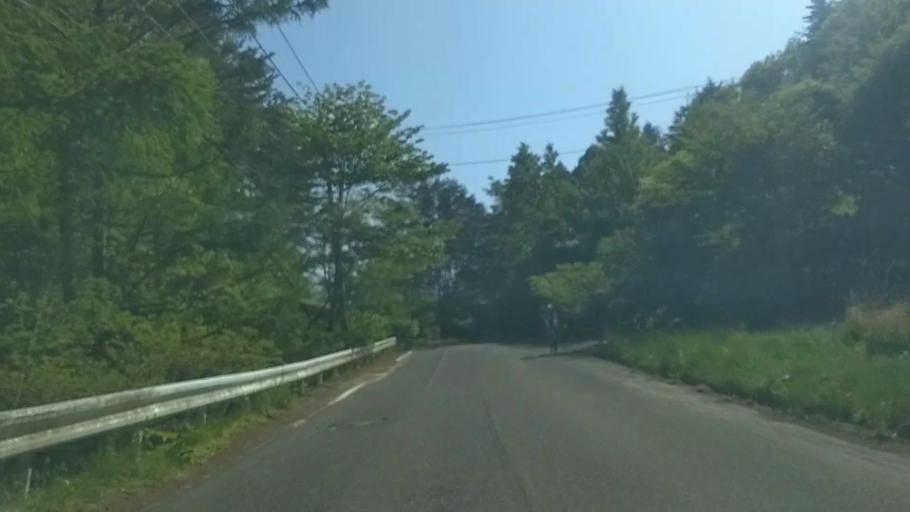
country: JP
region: Yamanashi
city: Nirasaki
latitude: 35.8920
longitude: 138.3986
